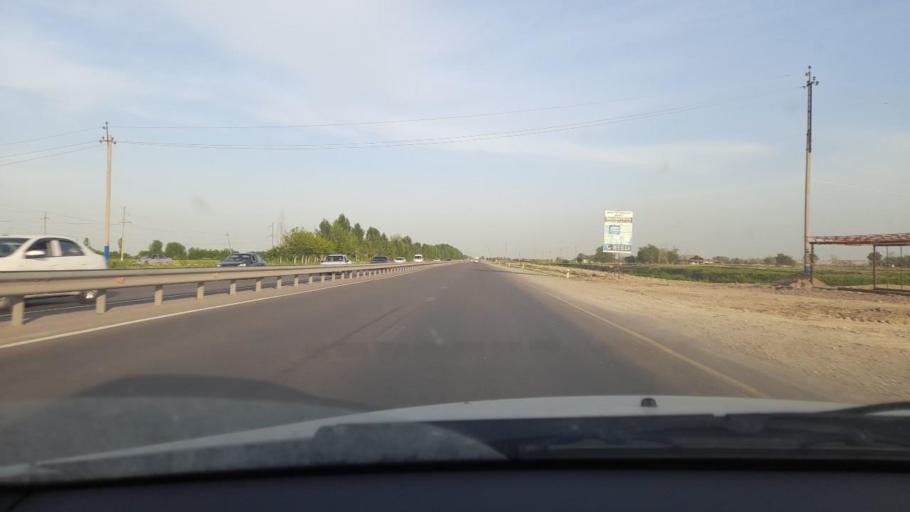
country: KZ
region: Ongtustik Qazaqstan
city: Myrzakent
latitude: 40.5360
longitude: 68.4288
